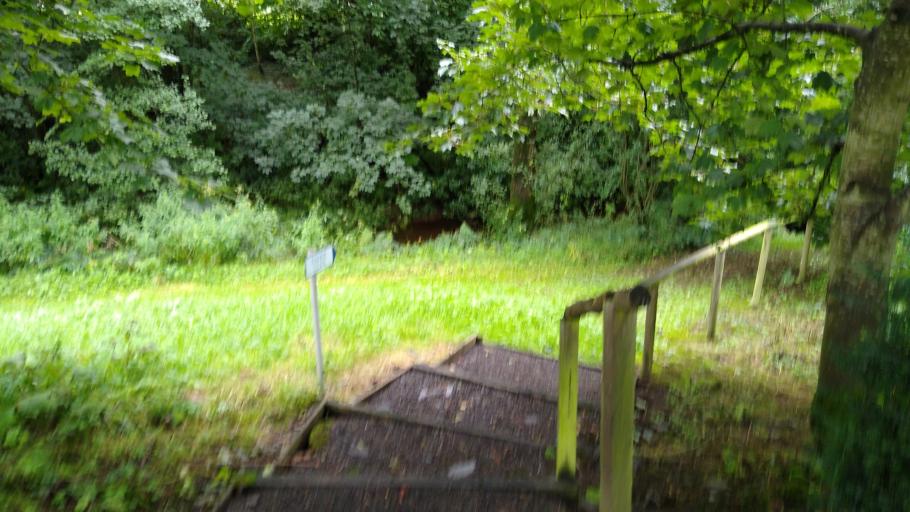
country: GB
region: England
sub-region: Cumbria
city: Scotby
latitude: 54.9979
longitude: -2.8834
